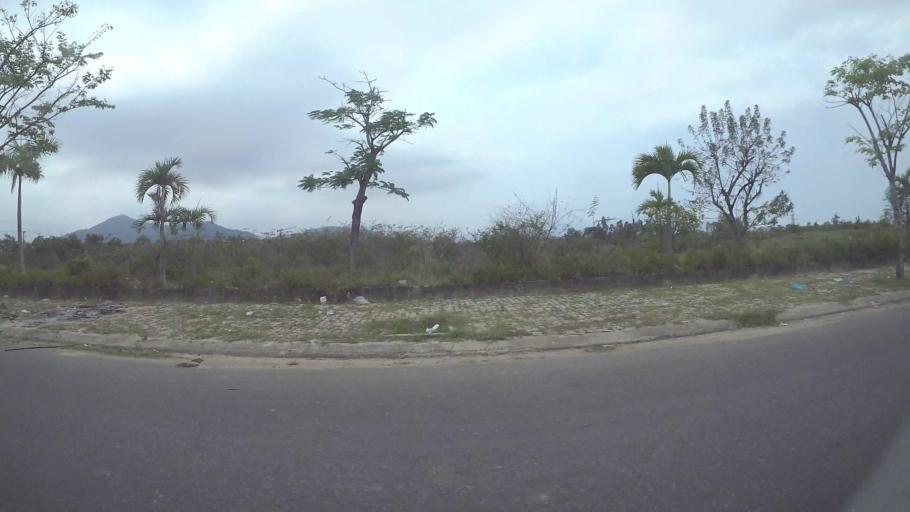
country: VN
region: Da Nang
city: Lien Chieu
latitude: 16.0478
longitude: 108.1649
